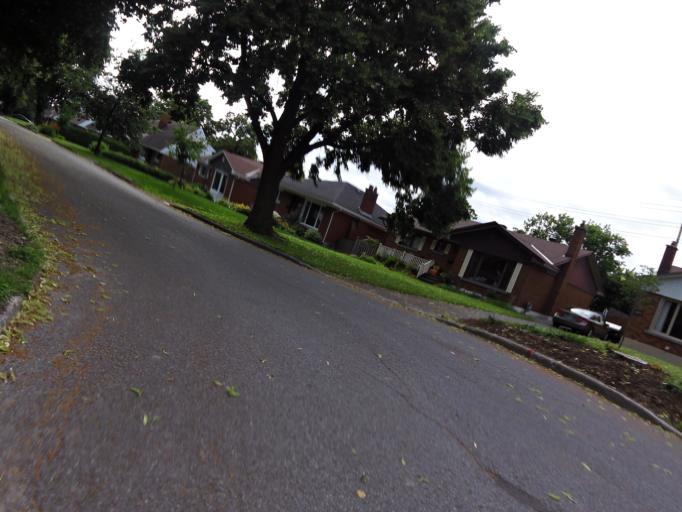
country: CA
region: Ontario
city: Bells Corners
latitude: 45.3530
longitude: -75.7906
